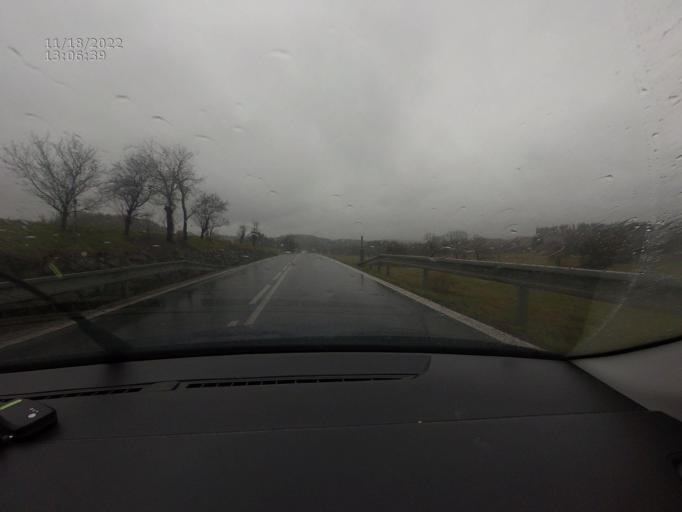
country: CZ
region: Plzensky
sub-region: Okres Klatovy
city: Planice
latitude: 49.3347
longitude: 13.4963
